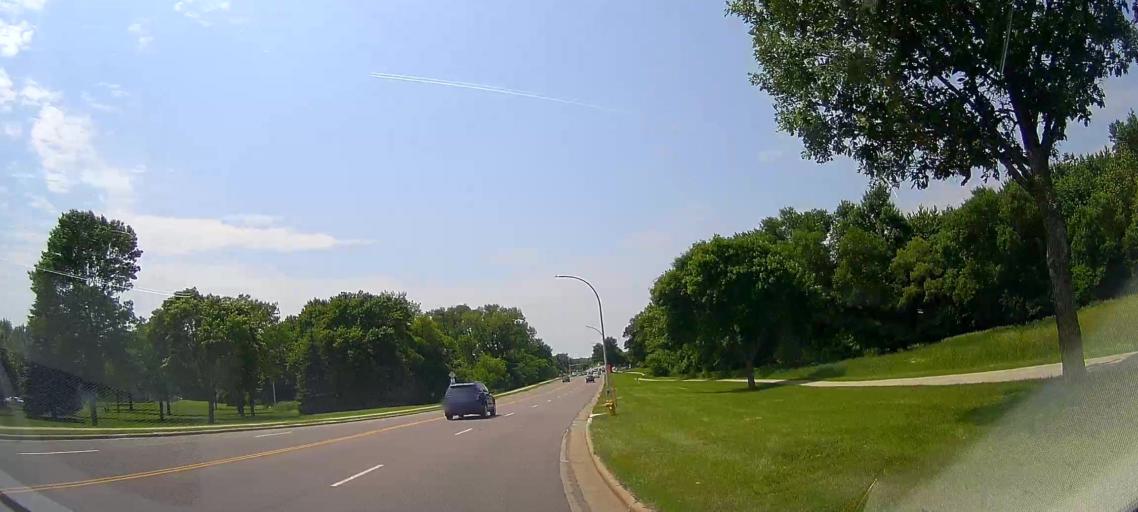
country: US
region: South Dakota
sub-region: Minnehaha County
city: Sioux Falls
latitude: 43.5078
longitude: -96.7612
